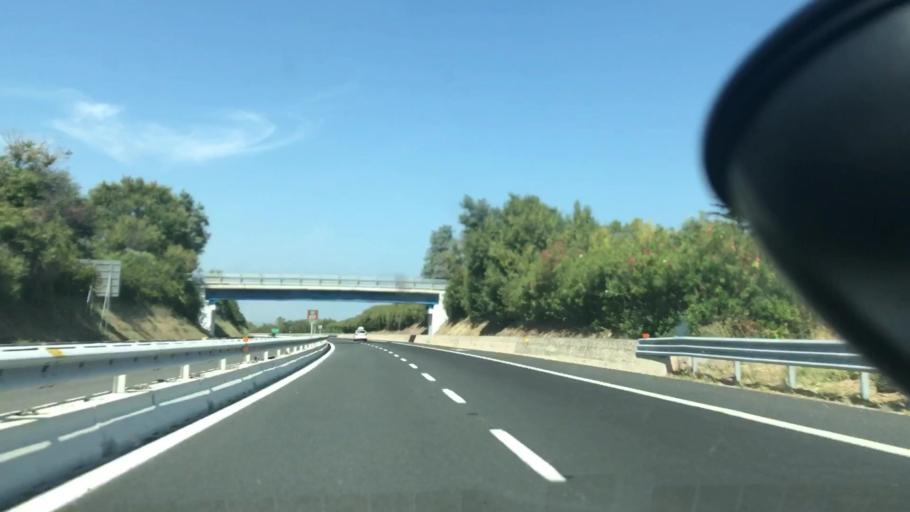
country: IT
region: Abruzzo
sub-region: Provincia di Chieti
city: Vasto
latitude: 42.1318
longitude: 14.6697
